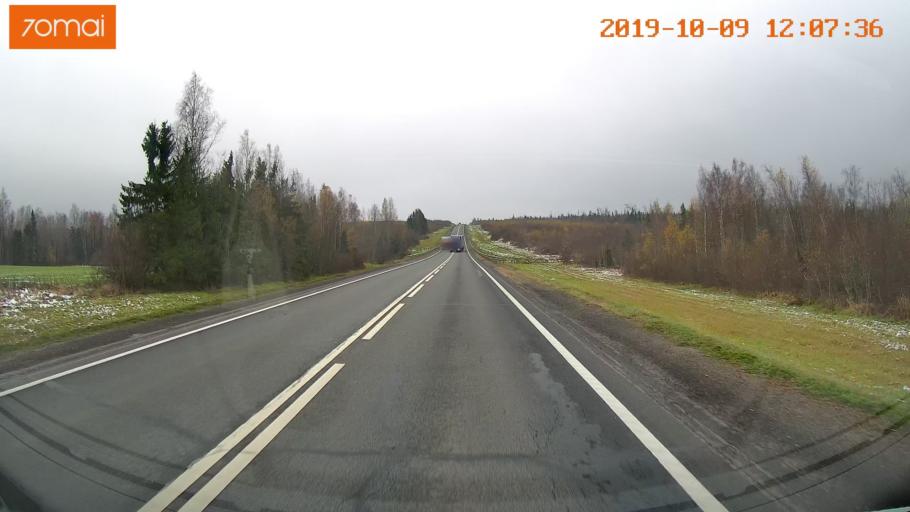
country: RU
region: Jaroslavl
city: Prechistoye
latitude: 58.5972
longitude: 40.3429
